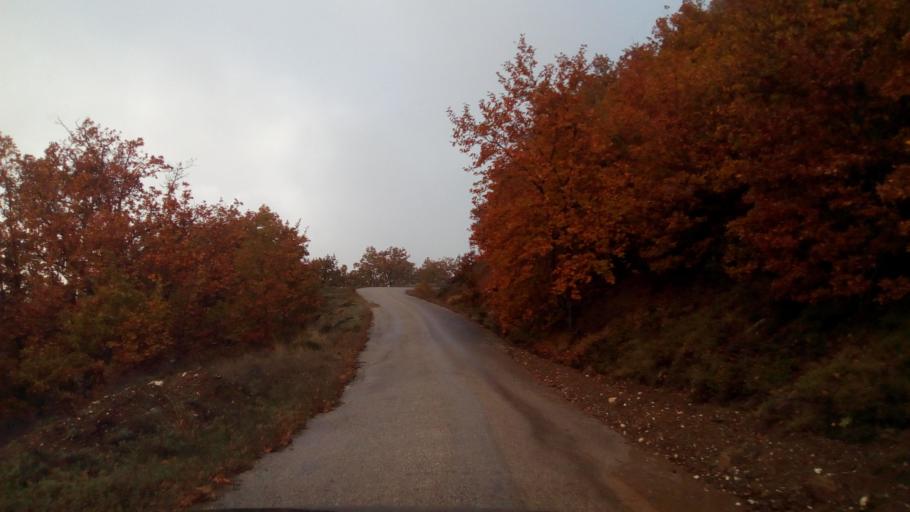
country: GR
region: West Greece
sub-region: Nomos Aitolias kai Akarnanias
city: Nafpaktos
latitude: 38.5495
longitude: 21.9284
